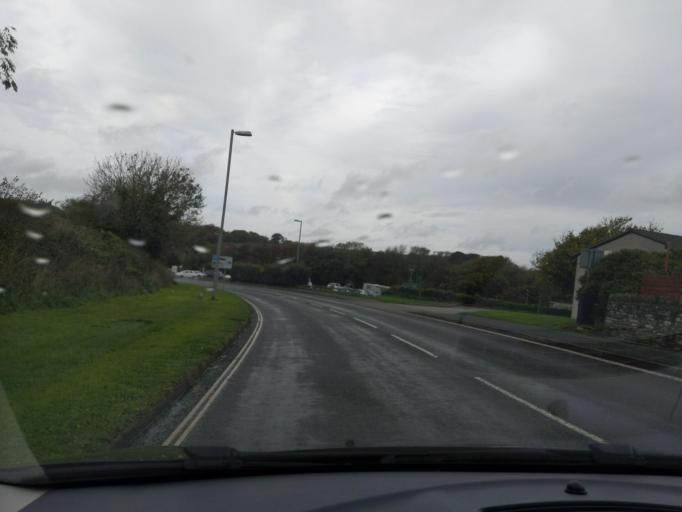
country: GB
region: England
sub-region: Cornwall
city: Padstow
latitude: 50.5389
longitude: -4.9413
